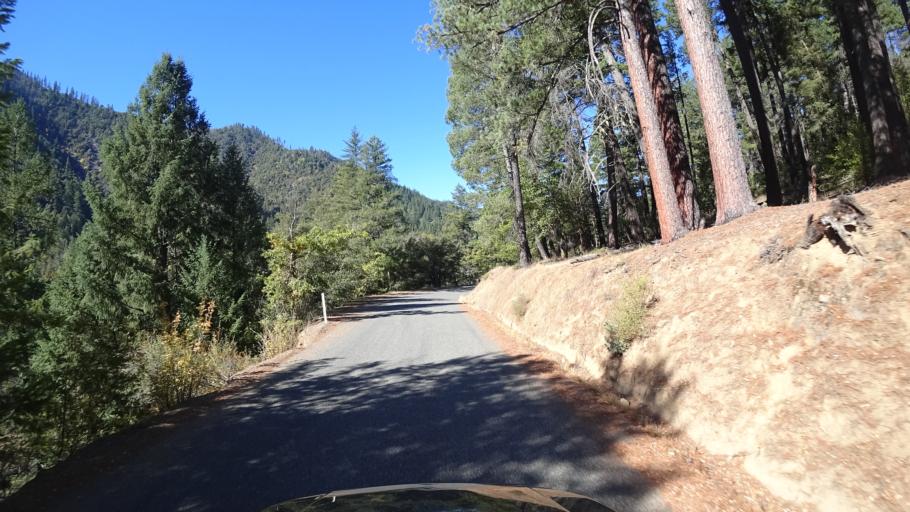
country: US
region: California
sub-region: Humboldt County
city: Willow Creek
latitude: 41.2776
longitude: -123.3463
